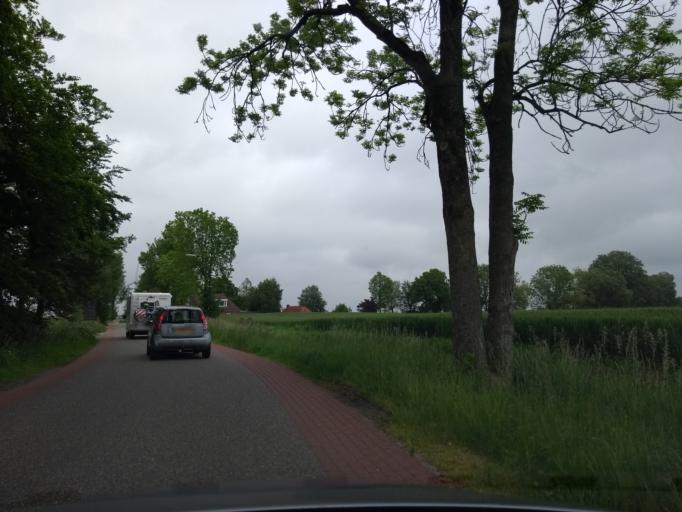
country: NL
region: Groningen
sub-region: Gemeente Zuidhorn
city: Oldehove
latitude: 53.3285
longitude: 6.4266
